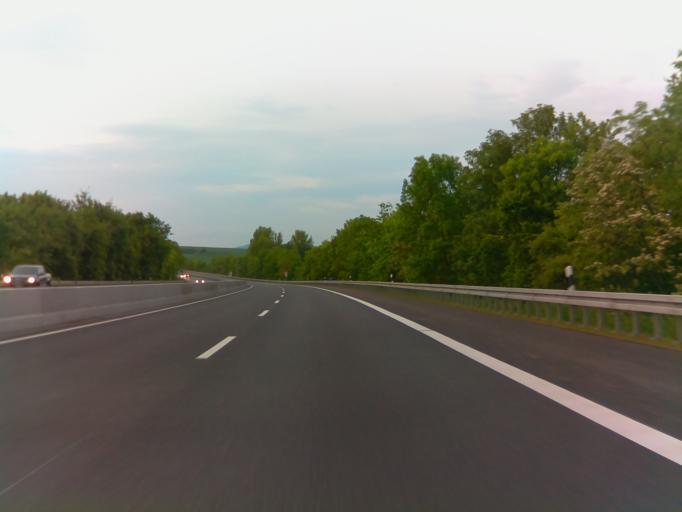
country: DE
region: Hesse
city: Fritzlar
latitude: 51.1170
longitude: 9.3065
